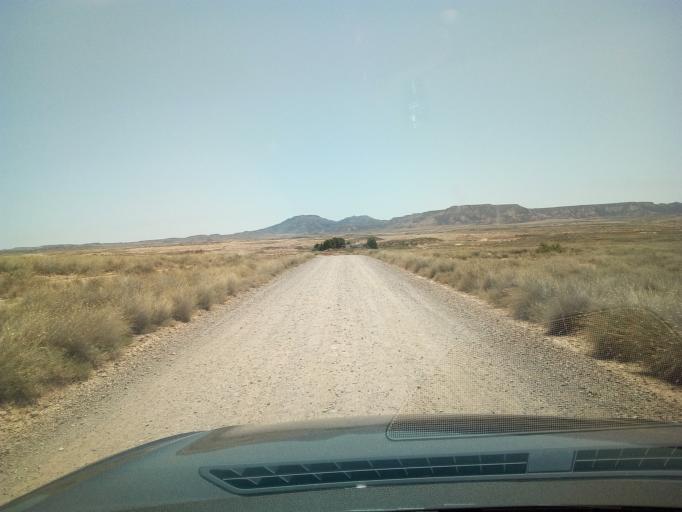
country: ES
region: Navarre
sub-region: Provincia de Navarra
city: Arguedas
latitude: 42.1844
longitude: -1.4818
